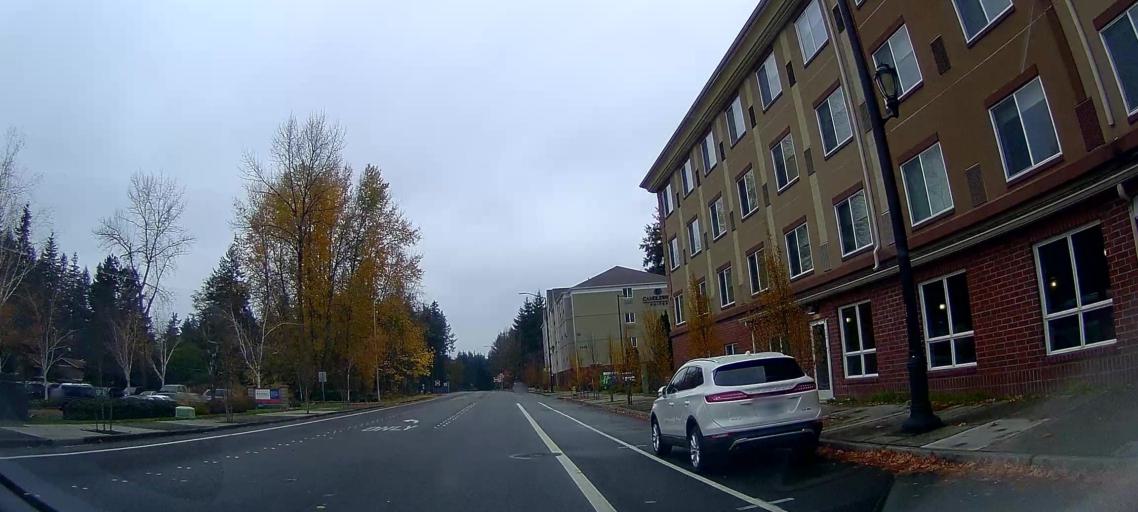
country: US
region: Washington
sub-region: Thurston County
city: Lacey
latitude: 47.0456
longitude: -122.8264
